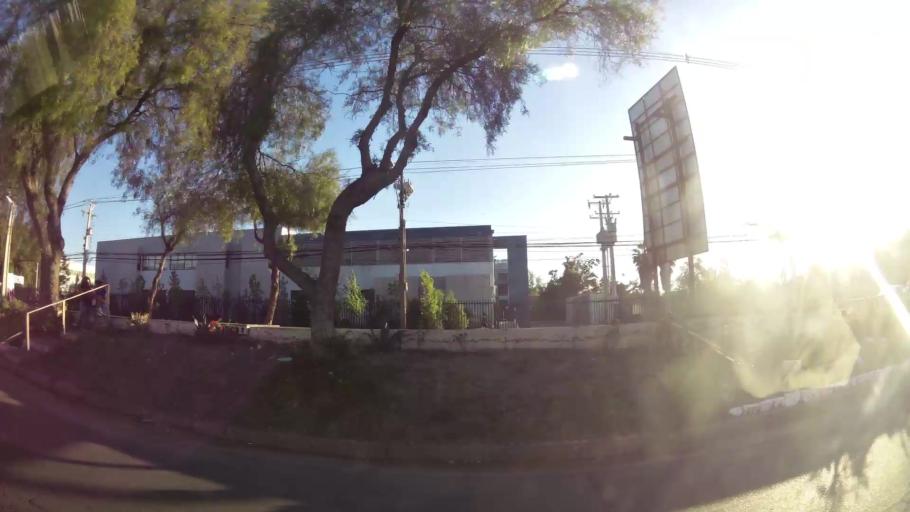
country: CL
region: Santiago Metropolitan
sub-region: Provincia de Maipo
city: San Bernardo
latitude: -33.6016
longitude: -70.6887
